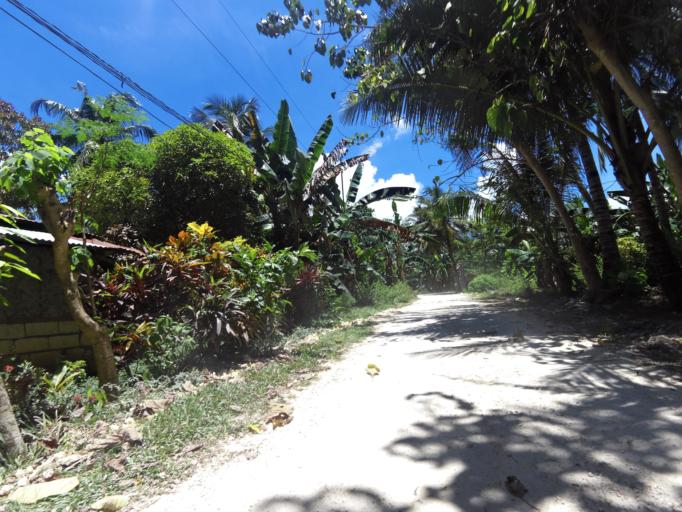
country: PH
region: Central Visayas
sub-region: Province of Bohol
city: Candabong
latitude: 9.7321
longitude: 124.5325
